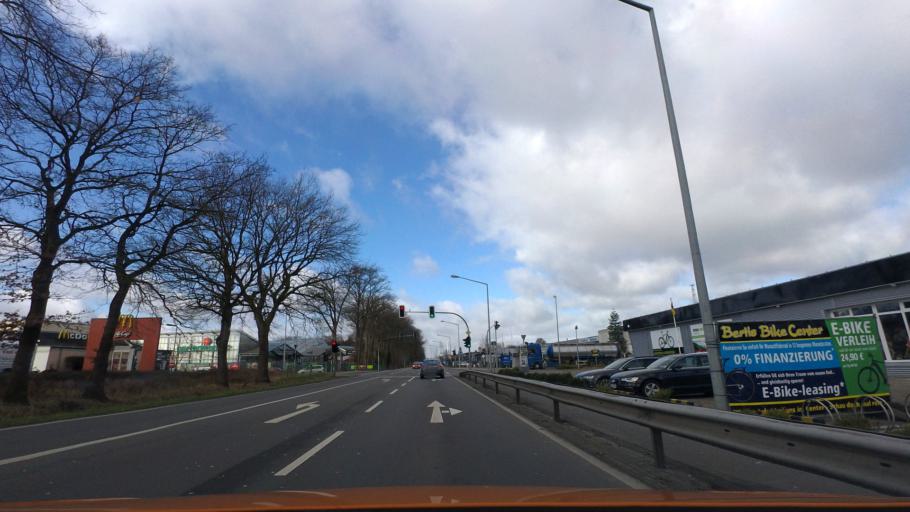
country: DE
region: Lower Saxony
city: Cloppenburg
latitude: 52.8404
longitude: 8.0690
